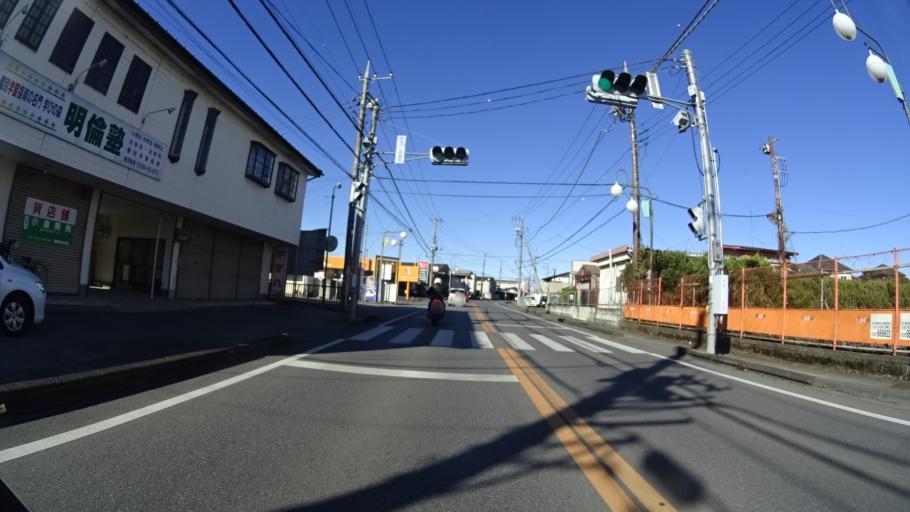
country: JP
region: Tochigi
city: Kanuma
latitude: 36.5527
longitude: 139.7469
